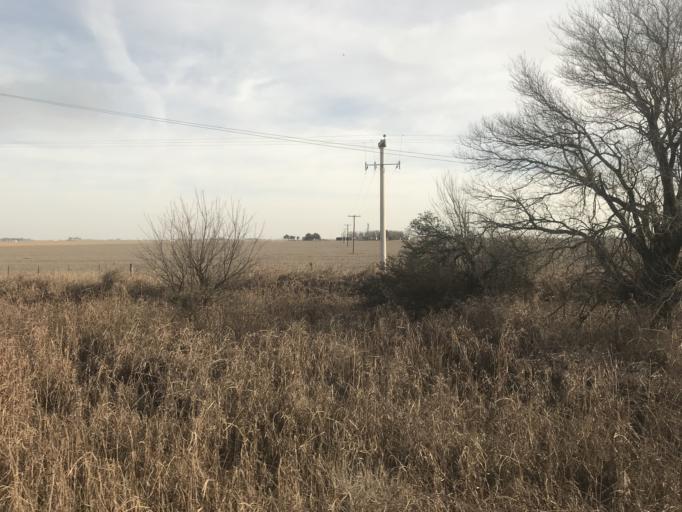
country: AR
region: Cordoba
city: Pilar
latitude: -31.7161
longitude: -63.8562
